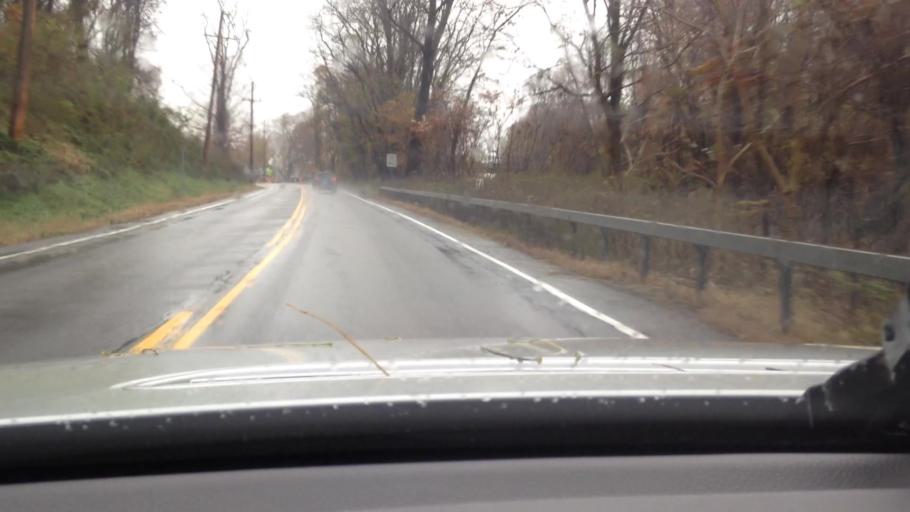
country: US
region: New York
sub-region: Putnam County
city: Cold Spring
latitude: 41.4279
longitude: -73.9668
